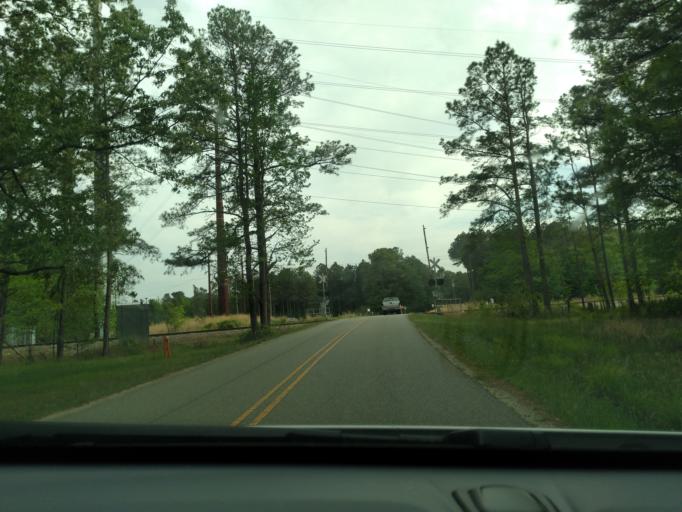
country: US
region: Virginia
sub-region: York County
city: Yorktown
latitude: 37.1737
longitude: -76.5150
